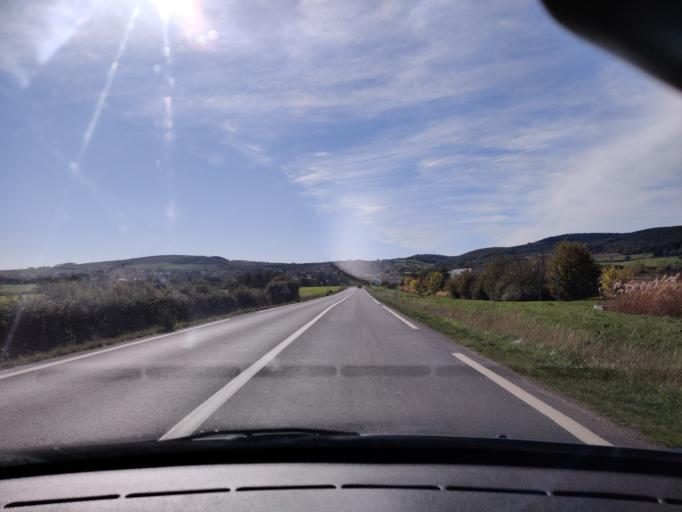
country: FR
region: Auvergne
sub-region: Departement du Puy-de-Dome
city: Combronde
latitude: 45.9964
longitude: 3.0916
